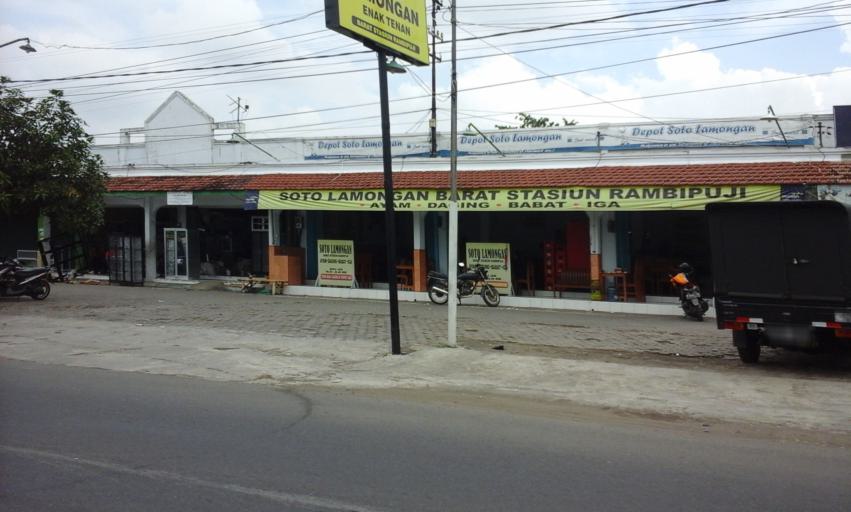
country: ID
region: East Java
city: Rambipuji
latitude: -8.2038
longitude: 113.6139
